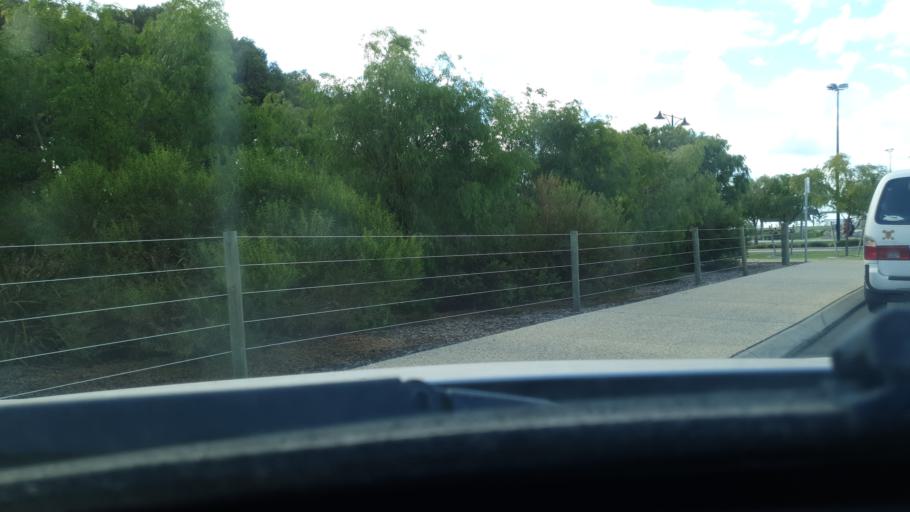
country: AU
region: Western Australia
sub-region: Busselton
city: Busselton
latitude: -33.6455
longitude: 115.3481
